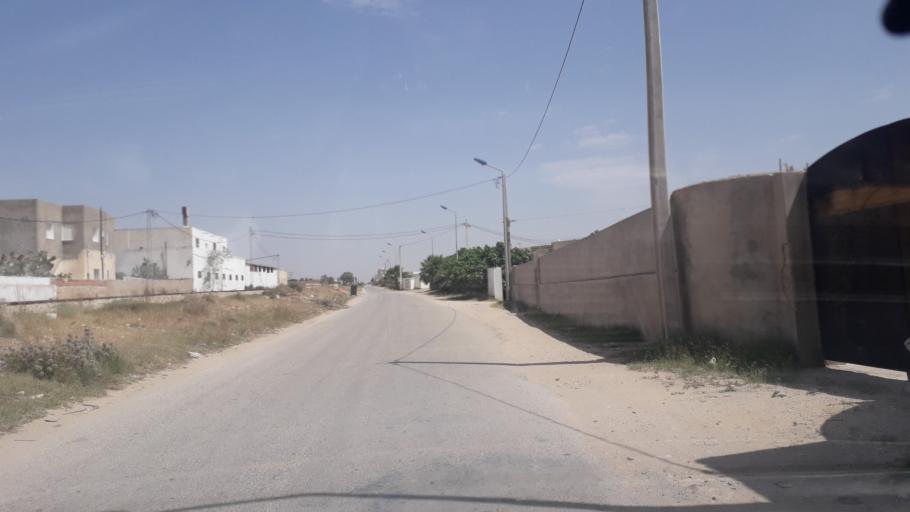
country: TN
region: Safaqis
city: Al Qarmadah
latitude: 34.8270
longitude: 10.7646
